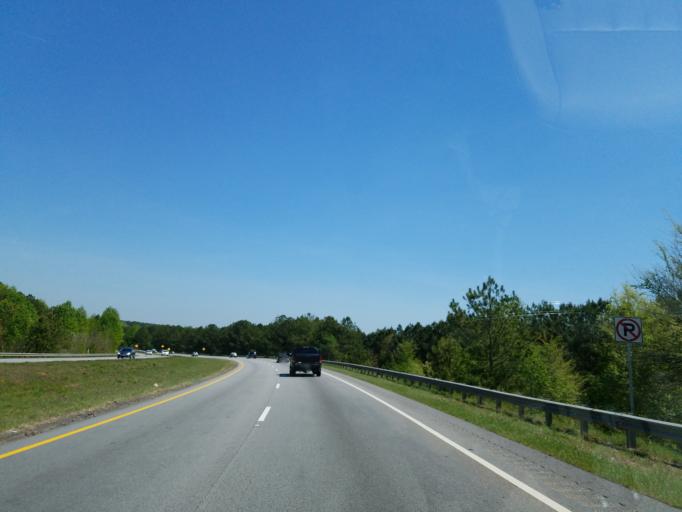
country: US
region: Georgia
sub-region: Paulding County
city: Dallas
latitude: 33.9021
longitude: -84.8084
